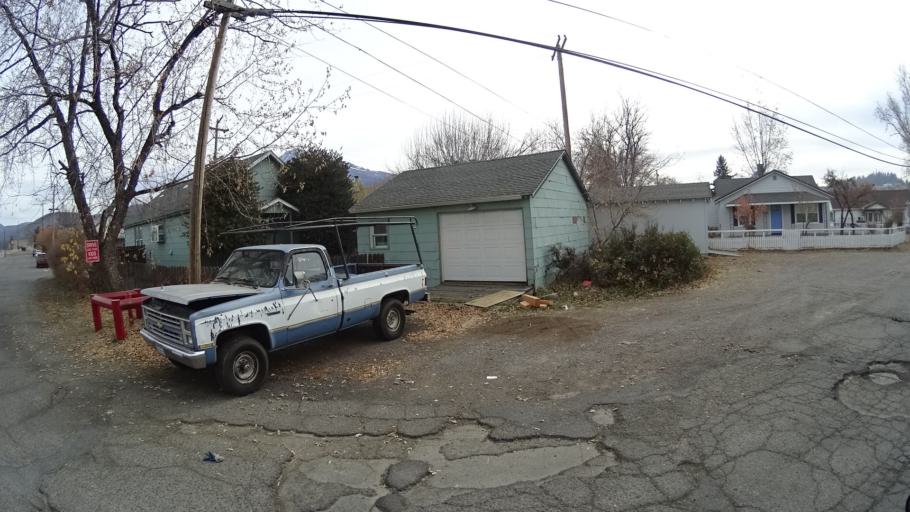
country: US
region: California
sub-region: Siskiyou County
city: Weed
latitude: 41.4331
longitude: -122.3782
